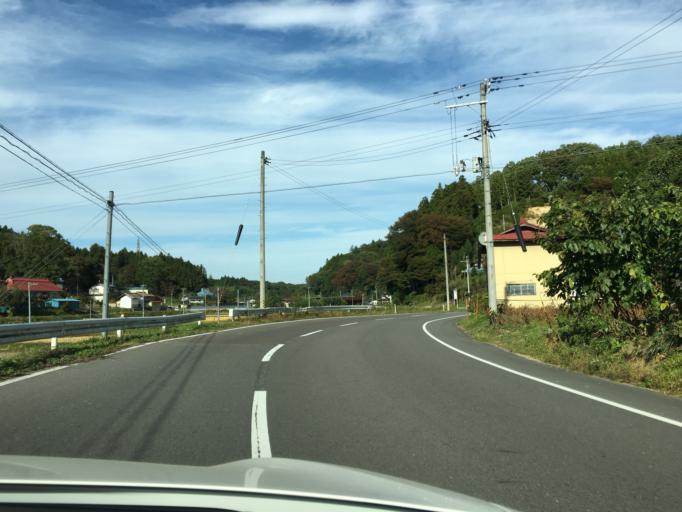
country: JP
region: Fukushima
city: Miharu
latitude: 37.3473
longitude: 140.5088
